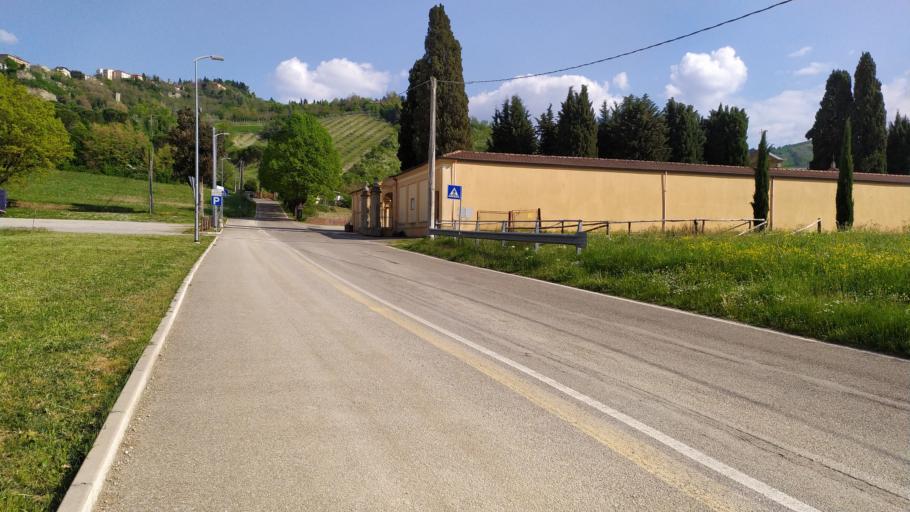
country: IT
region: Emilia-Romagna
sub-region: Provincia di Bologna
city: Borgo Tossignano
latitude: 44.2760
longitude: 11.5946
